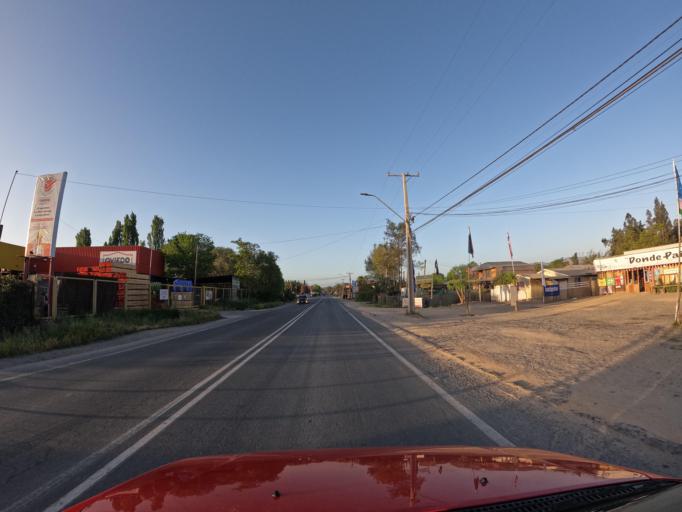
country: CL
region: O'Higgins
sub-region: Provincia de Cachapoal
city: San Vicente
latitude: -34.1736
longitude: -71.3975
